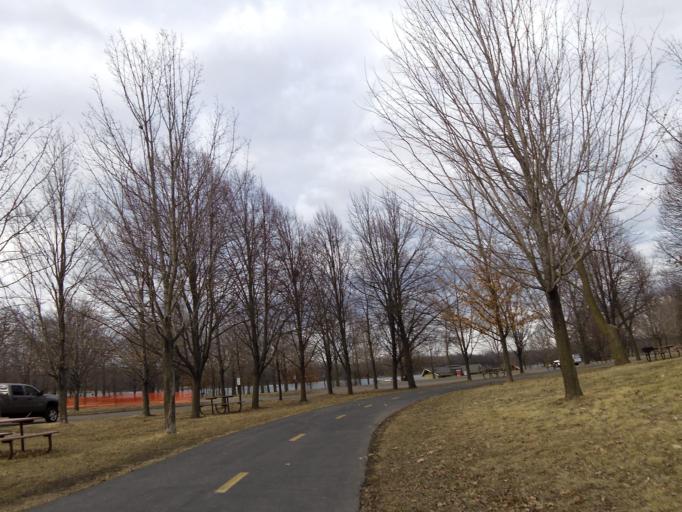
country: US
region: Minnesota
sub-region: Scott County
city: Prior Lake
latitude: 44.6899
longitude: -93.3881
